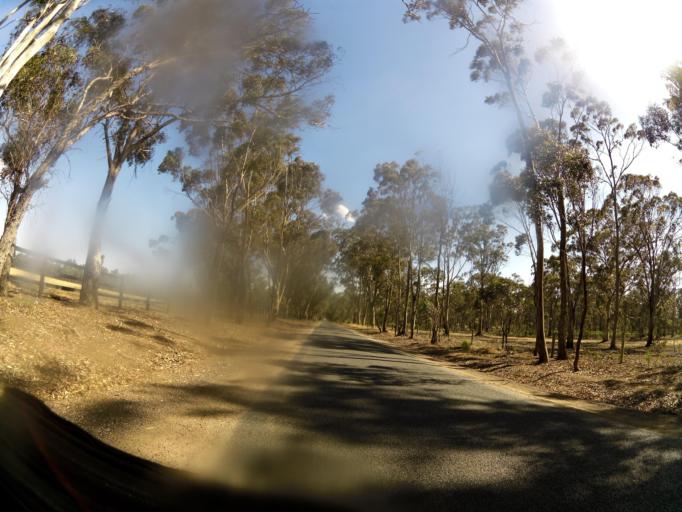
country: AU
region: Victoria
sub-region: Campaspe
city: Kyabram
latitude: -36.8665
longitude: 145.0872
